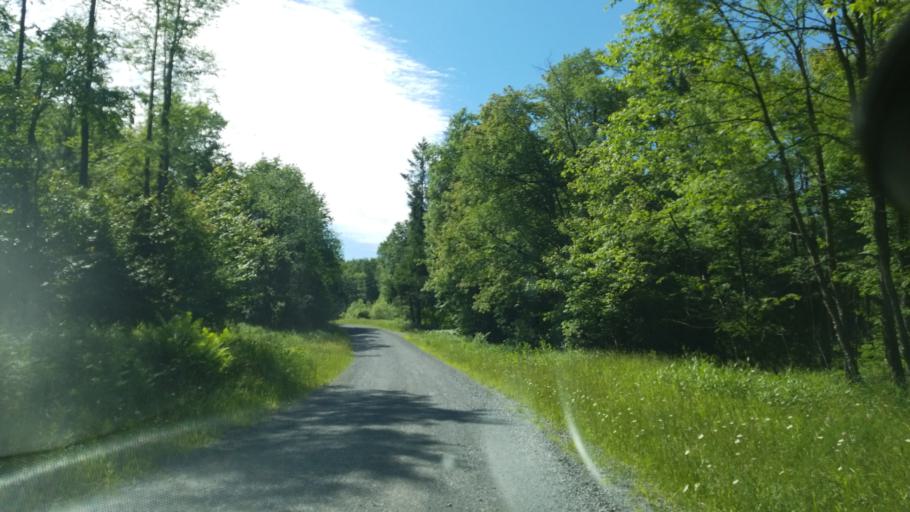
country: US
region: Pennsylvania
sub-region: Clearfield County
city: Clearfield
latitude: 41.1887
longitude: -78.4665
